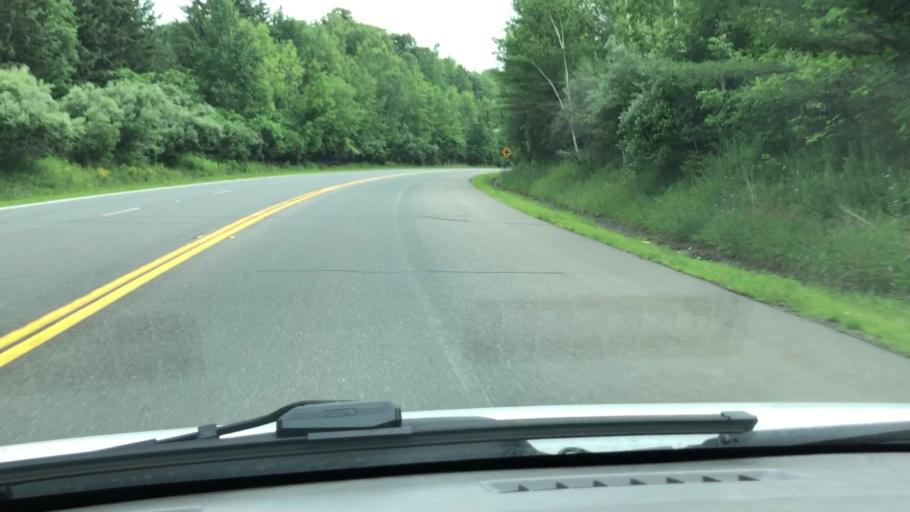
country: US
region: Massachusetts
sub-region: Berkshire County
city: Adams
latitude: 42.5916
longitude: -73.1461
